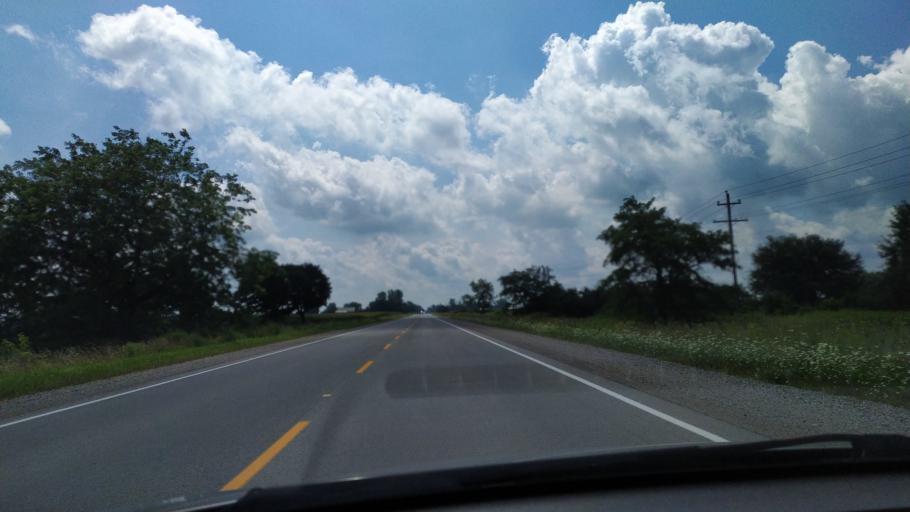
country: CA
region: Ontario
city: London
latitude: 43.1409
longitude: -81.3419
